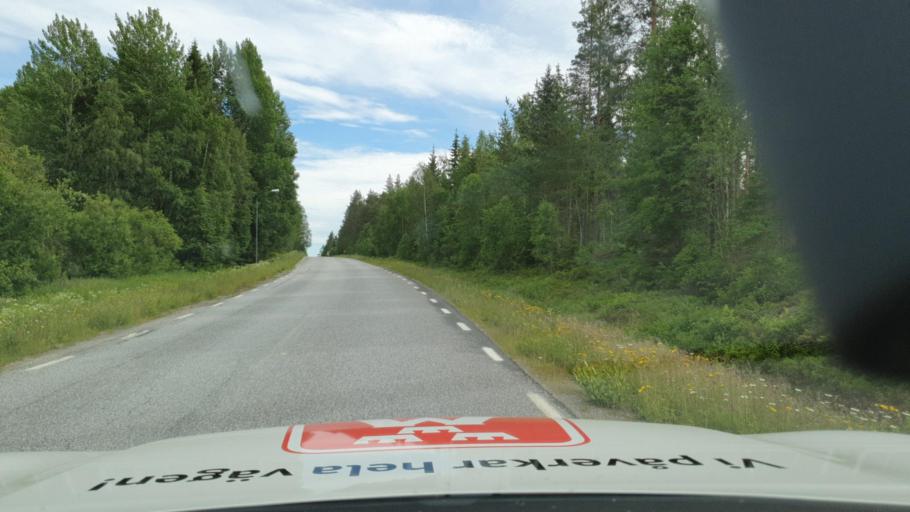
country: SE
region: Vaesterbotten
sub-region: Skelleftea Kommun
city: Burea
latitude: 64.4862
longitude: 21.0357
